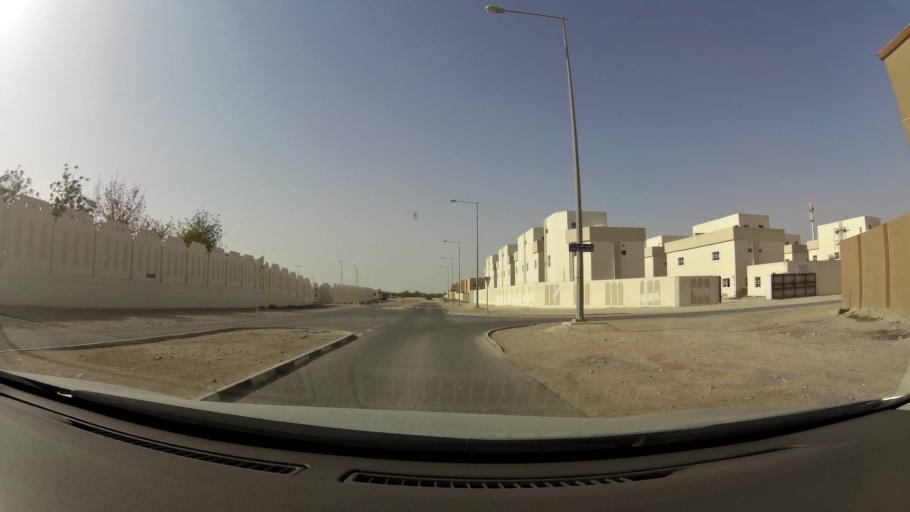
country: QA
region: Baladiyat ar Rayyan
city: Ar Rayyan
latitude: 25.3460
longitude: 51.4240
